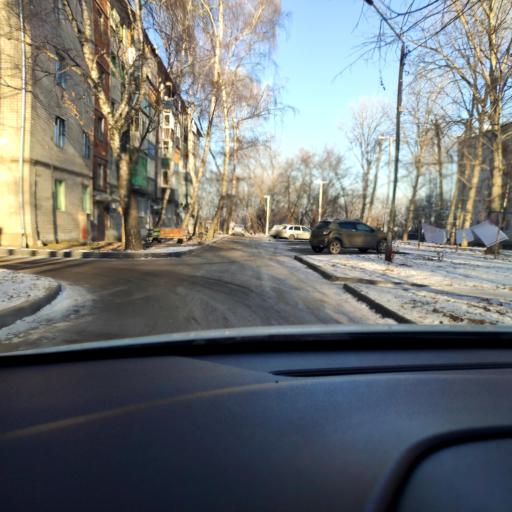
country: RU
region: Tatarstan
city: Staroye Arakchino
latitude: 55.8784
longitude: 49.0171
